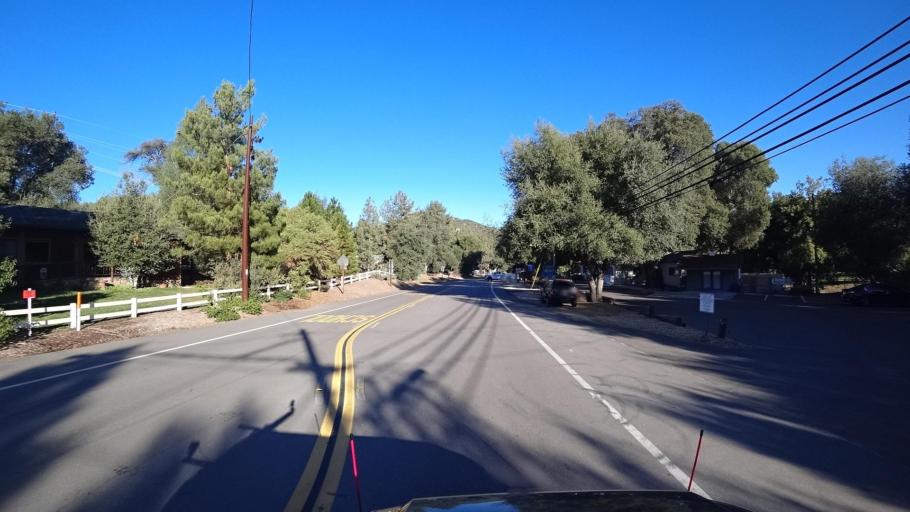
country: US
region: California
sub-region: San Diego County
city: Pine Valley
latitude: 32.8231
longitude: -116.5312
